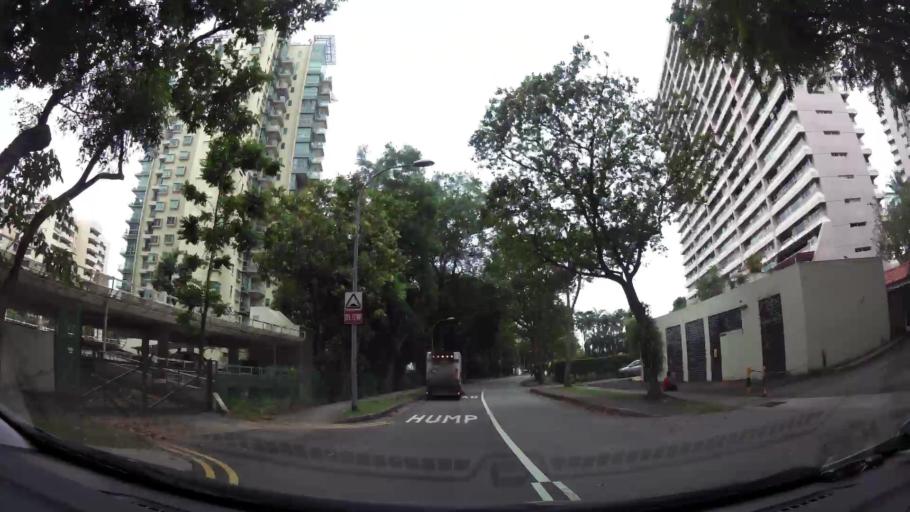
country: SG
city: Singapore
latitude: 1.3184
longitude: 103.7791
